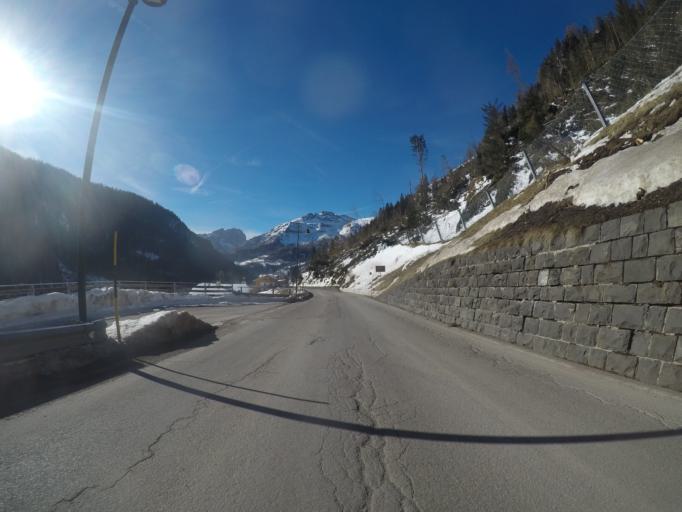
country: IT
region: Veneto
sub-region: Provincia di Belluno
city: Livinallongo del Col di Lana
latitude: 46.4853
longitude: 11.9836
